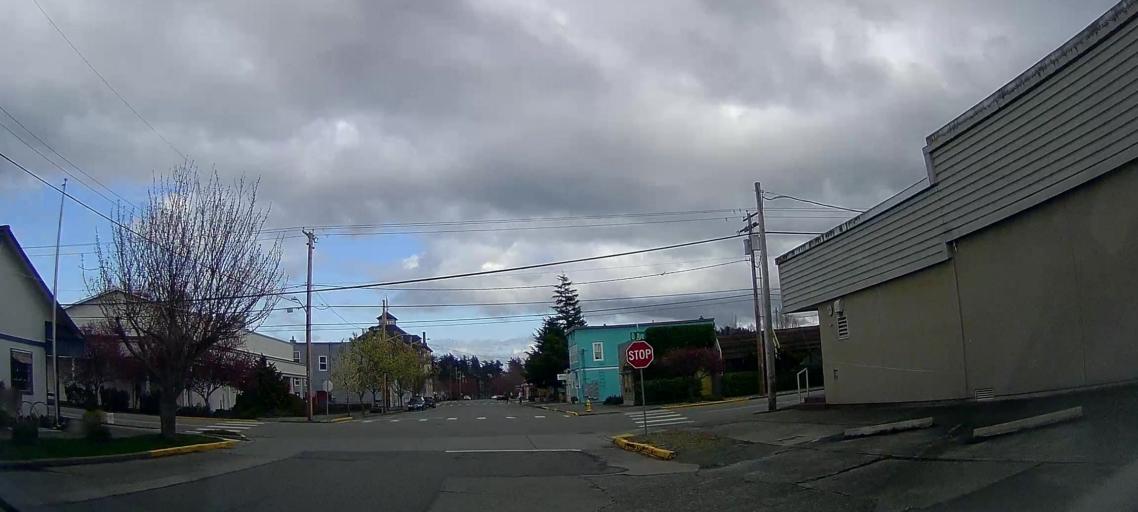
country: US
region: Washington
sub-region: Skagit County
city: Anacortes
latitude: 48.5185
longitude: -122.6147
